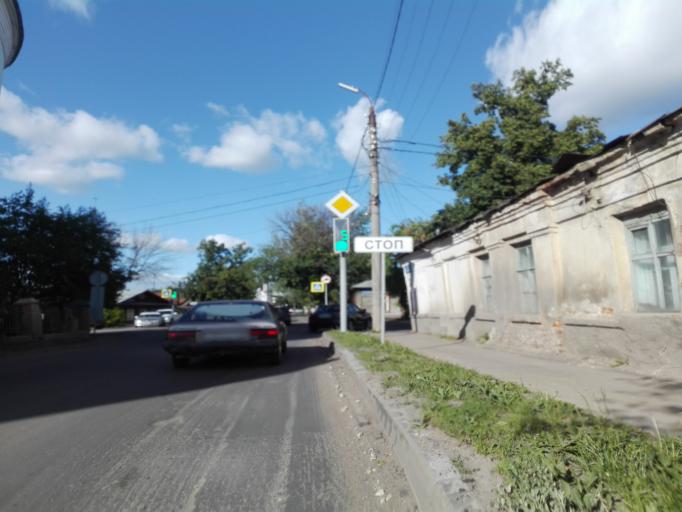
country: RU
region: Orjol
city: Orel
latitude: 52.9595
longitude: 36.0590
